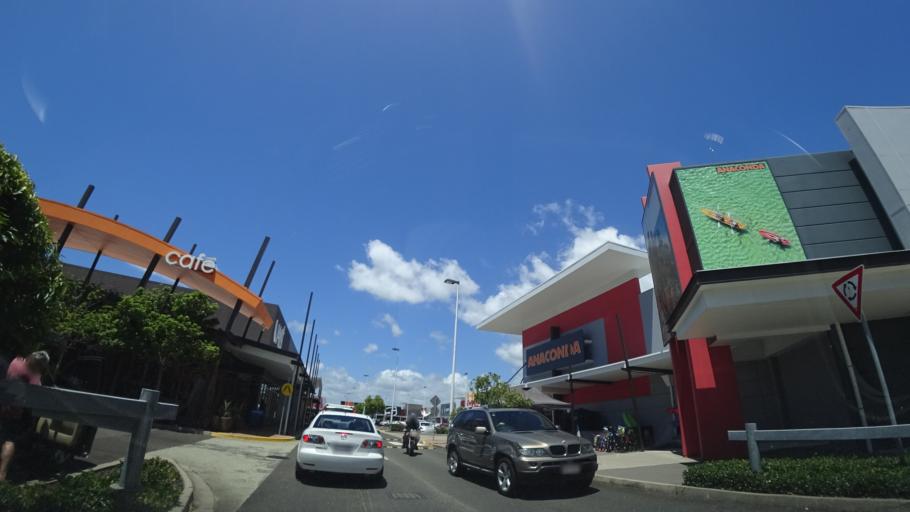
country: AU
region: Queensland
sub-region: Sunshine Coast
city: Dicky Beach
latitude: -26.7362
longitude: 153.1197
